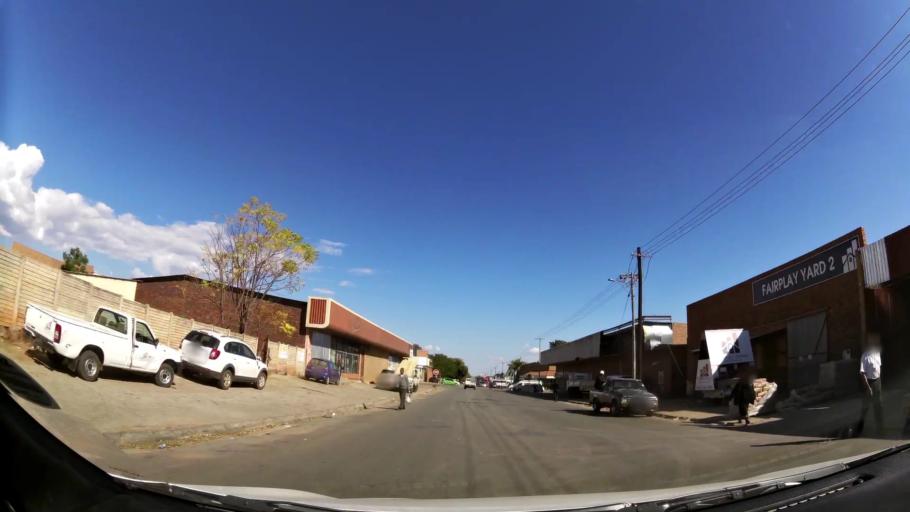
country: ZA
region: Limpopo
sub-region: Waterberg District Municipality
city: Mokopane
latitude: -24.1807
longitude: 29.0162
